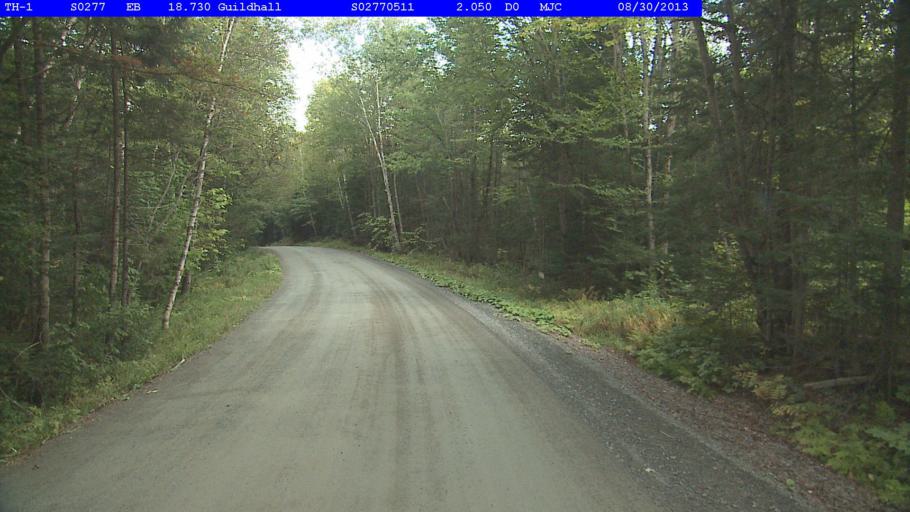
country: US
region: Vermont
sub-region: Essex County
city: Guildhall
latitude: 44.5618
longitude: -71.6345
